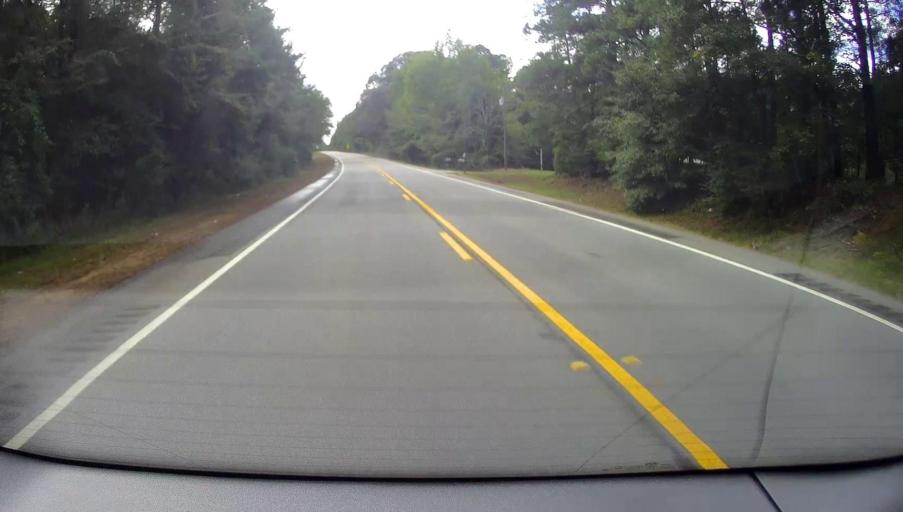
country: US
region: Georgia
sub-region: Baldwin County
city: Milledgeville
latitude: 33.0188
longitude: -83.3362
